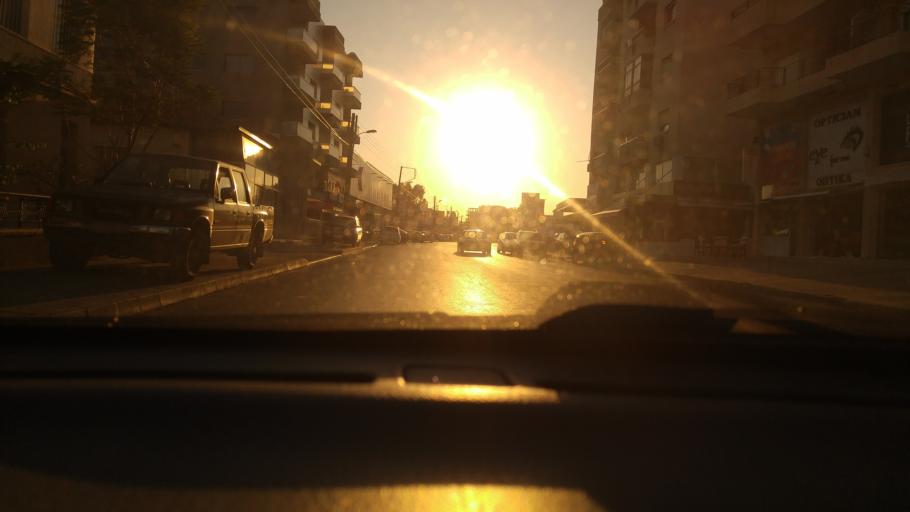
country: CY
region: Limassol
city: Limassol
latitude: 34.6740
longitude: 33.0242
